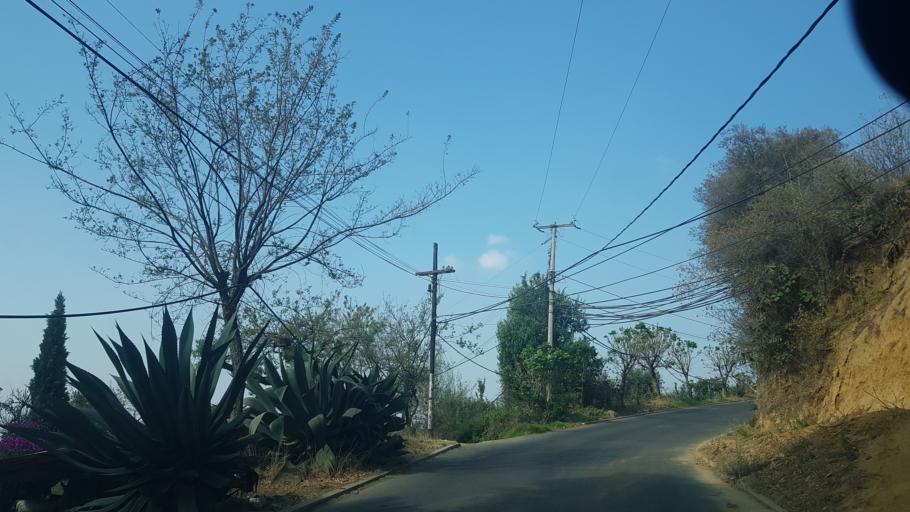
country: MX
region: Puebla
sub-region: Tochimilco
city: Santa Cruz Cuautomatitla
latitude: 18.8879
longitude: -98.6597
